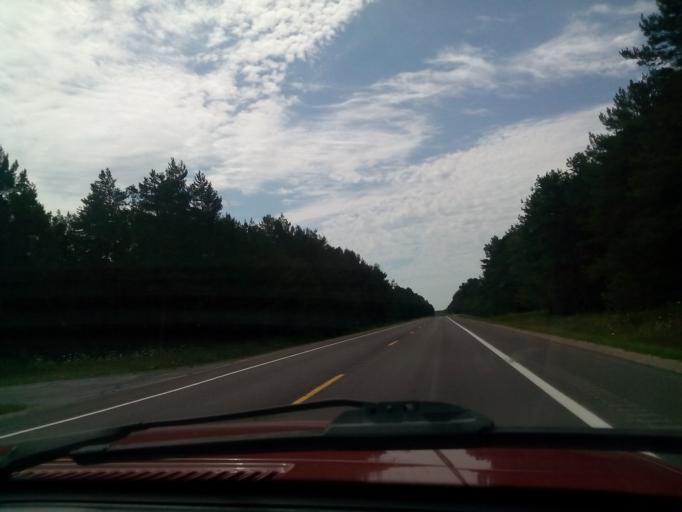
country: US
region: Michigan
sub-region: Schoolcraft County
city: Manistique
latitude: 46.0526
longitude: -85.9638
